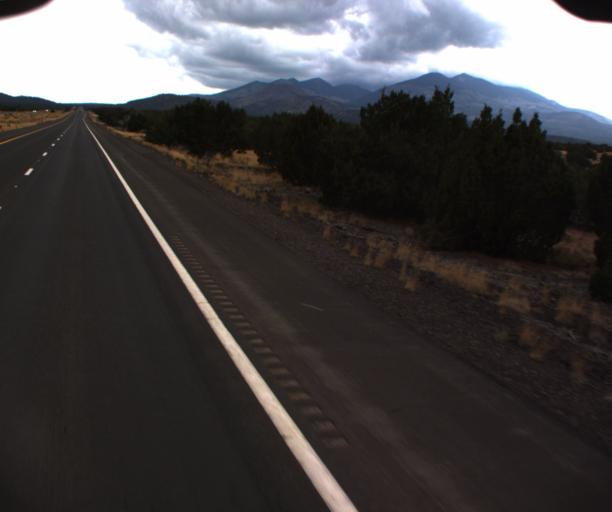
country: US
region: Arizona
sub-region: Coconino County
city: Flagstaff
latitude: 35.4264
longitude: -111.5696
